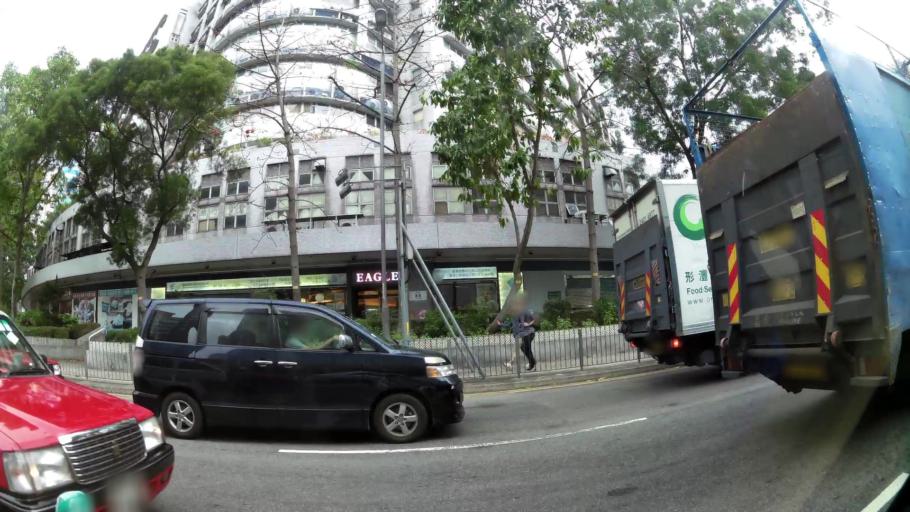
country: HK
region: Tsuen Wan
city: Tsuen Wan
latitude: 22.3701
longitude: 114.1339
